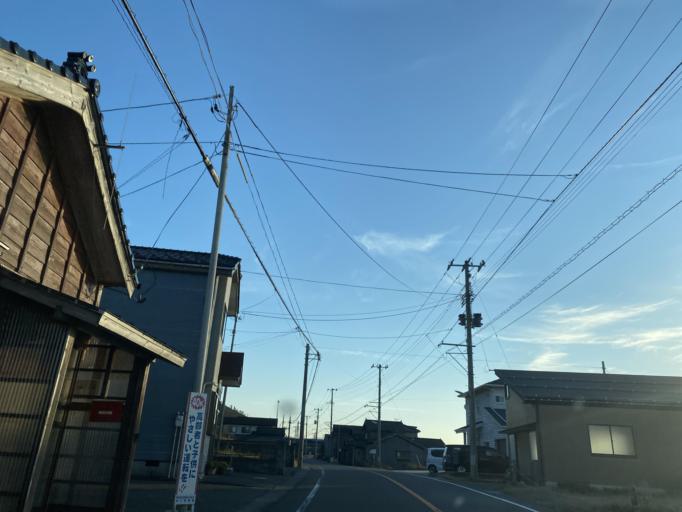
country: JP
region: Niigata
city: Kashiwazaki
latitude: 37.4613
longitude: 138.6118
